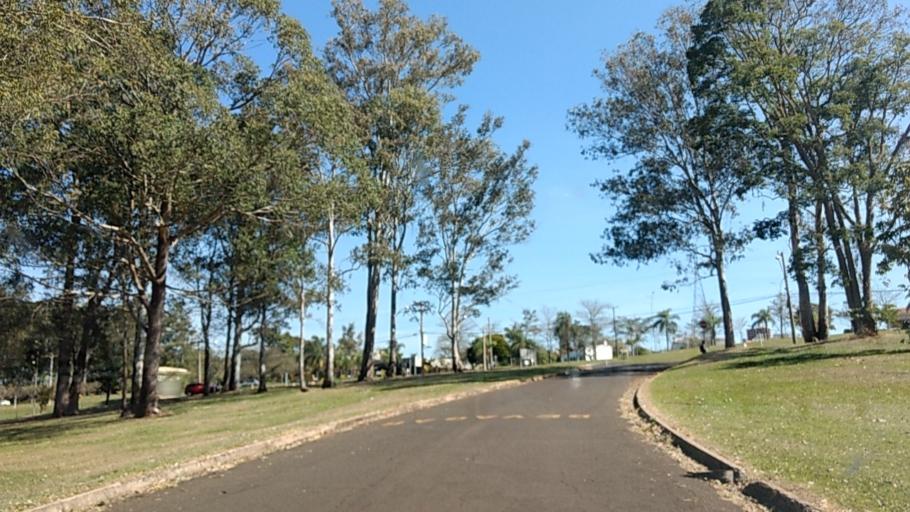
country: BR
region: Sao Paulo
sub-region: Botucatu
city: Botucatu
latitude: -22.8507
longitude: -48.4327
